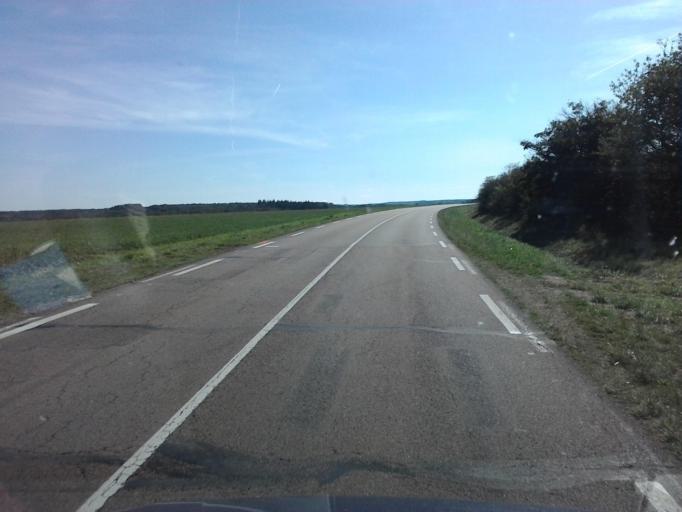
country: FR
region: Bourgogne
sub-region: Departement de la Cote-d'Or
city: Saulieu
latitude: 47.4072
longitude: 4.1548
